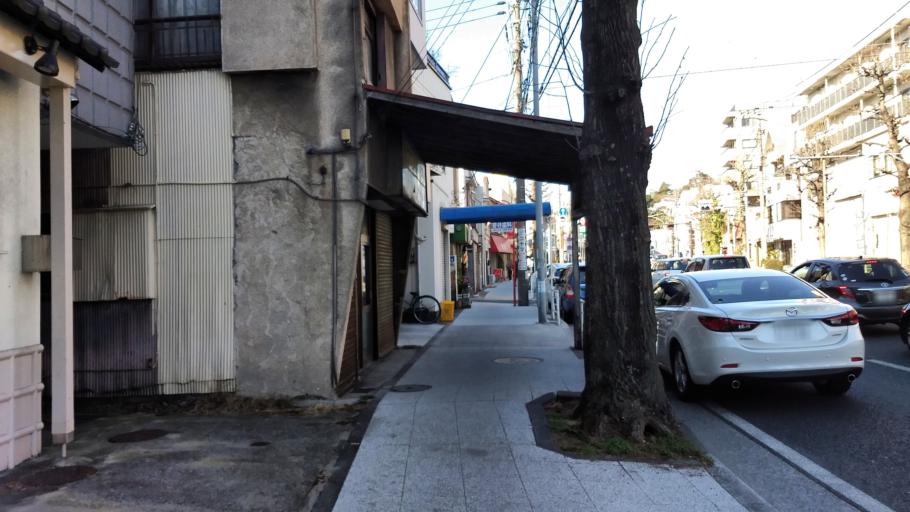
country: JP
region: Kanagawa
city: Yokohama
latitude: 35.4330
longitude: 139.6480
